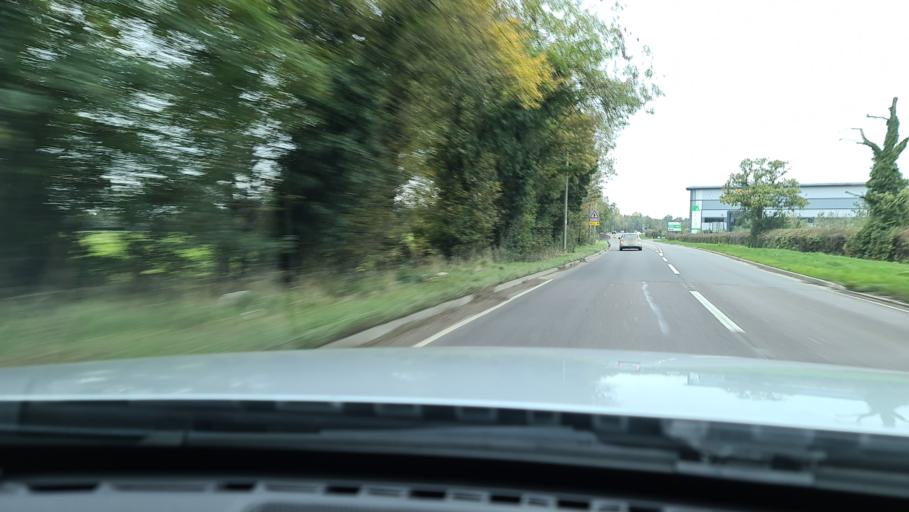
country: GB
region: England
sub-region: Oxfordshire
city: Bicester
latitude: 51.8795
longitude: -1.1229
